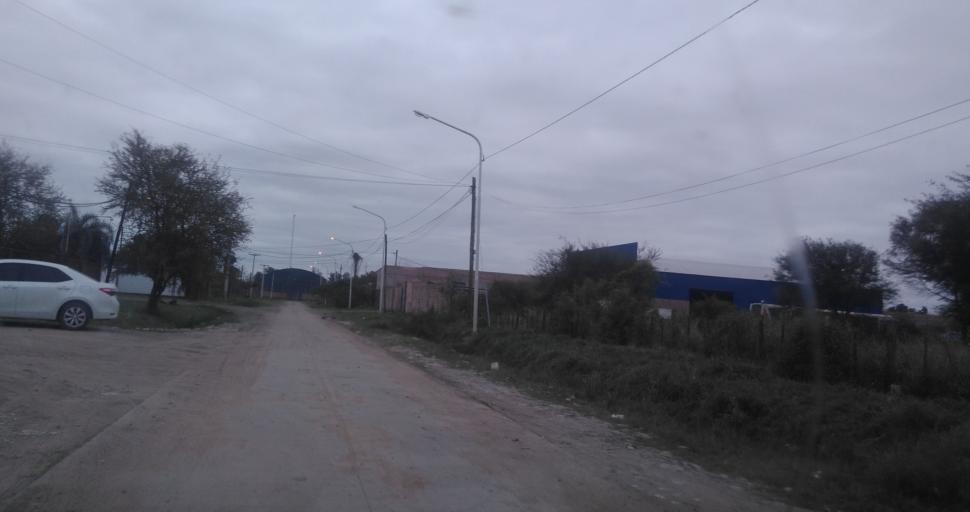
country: AR
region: Chaco
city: Fontana
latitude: -27.4342
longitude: -59.0276
